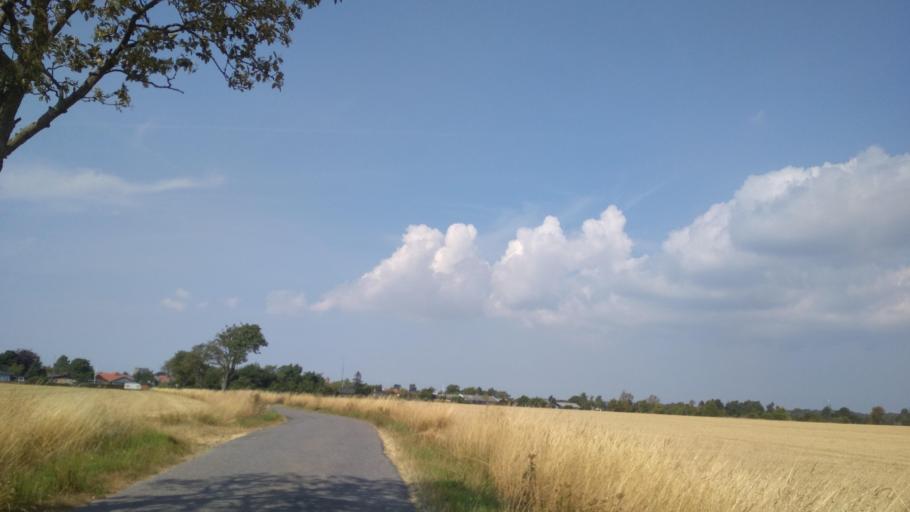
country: DK
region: Capital Region
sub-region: Bornholm Kommune
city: Akirkeby
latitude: 55.0662
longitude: 14.9330
